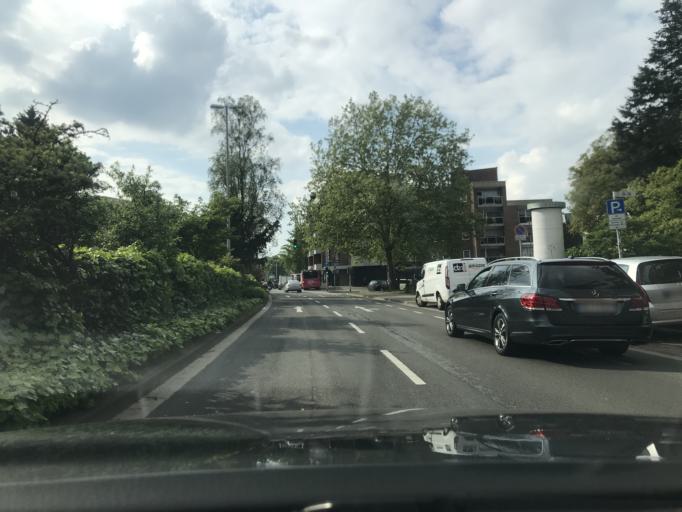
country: DE
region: North Rhine-Westphalia
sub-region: Regierungsbezirk Dusseldorf
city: Monchengladbach
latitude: 51.1966
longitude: 6.4323
